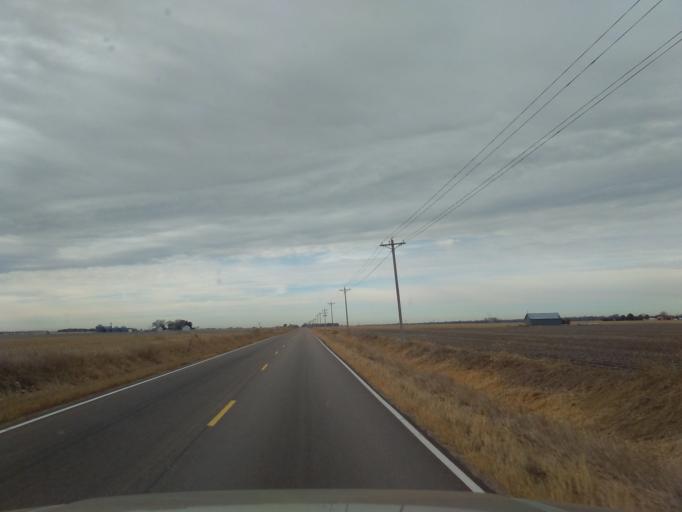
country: US
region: Nebraska
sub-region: Buffalo County
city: Gibbon
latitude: 40.6409
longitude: -98.9205
